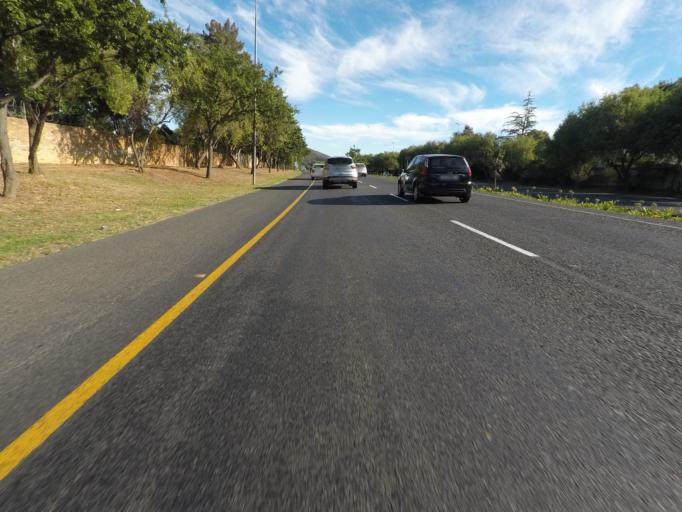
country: ZA
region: Western Cape
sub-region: Cape Winelands District Municipality
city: Stellenbosch
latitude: -33.9524
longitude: 18.8555
